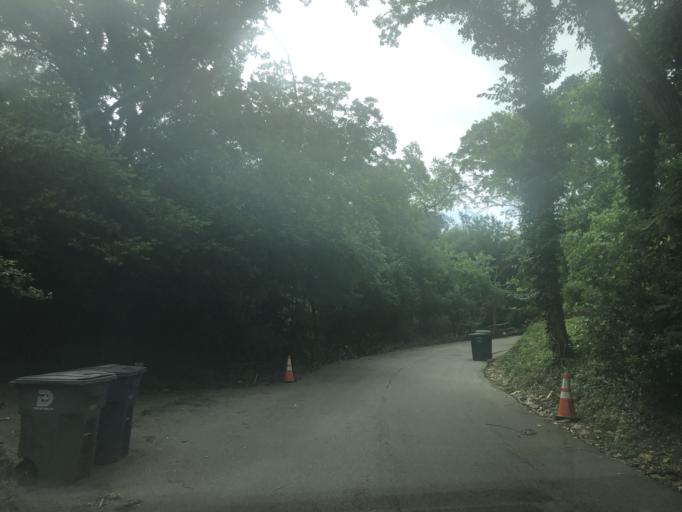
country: US
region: Texas
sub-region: Dallas County
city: University Park
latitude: 32.8590
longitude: -96.8359
